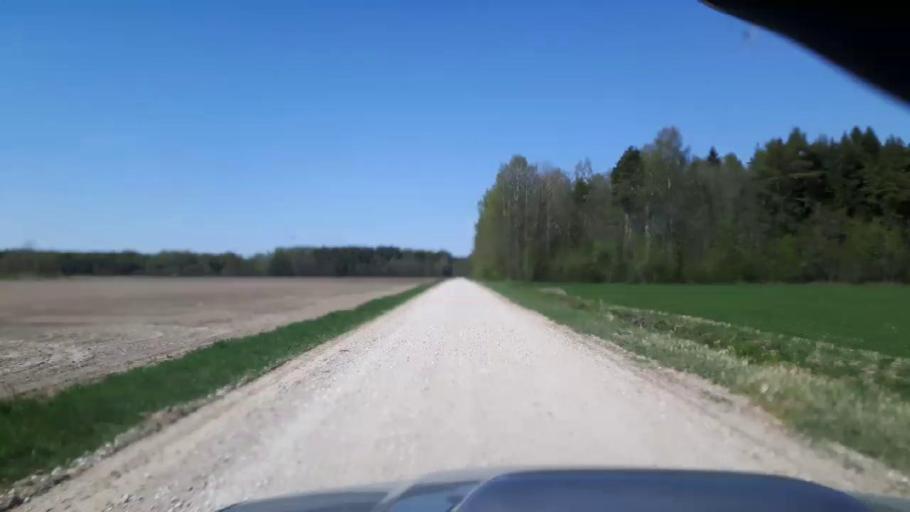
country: EE
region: Paernumaa
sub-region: Tootsi vald
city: Tootsi
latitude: 58.4704
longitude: 24.7695
